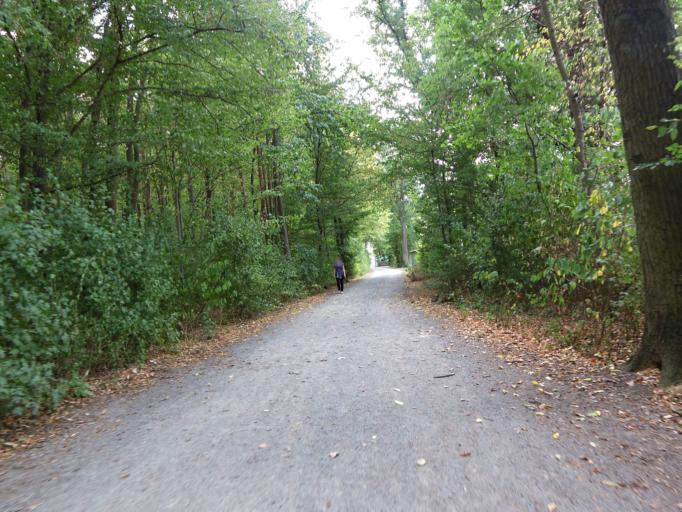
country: DE
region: Bavaria
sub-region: Regierungsbezirk Unterfranken
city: Gadheim
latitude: 49.8349
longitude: 9.8978
